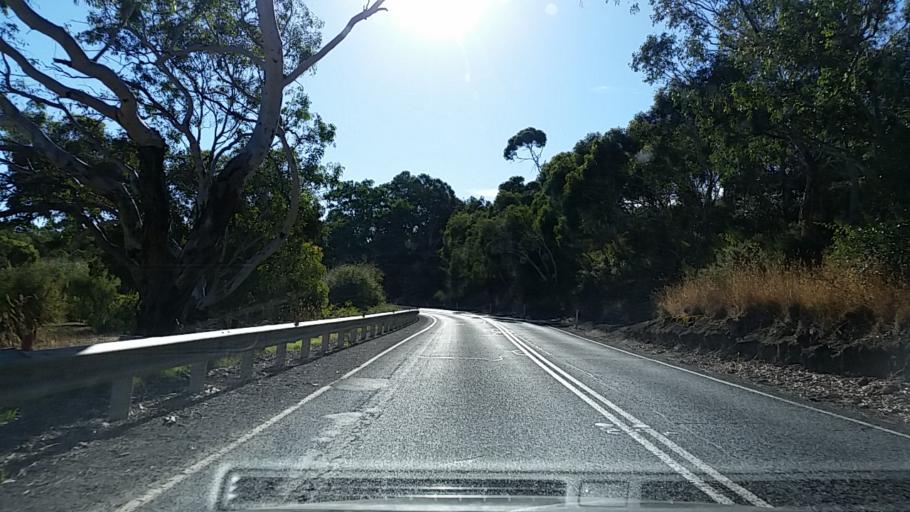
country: AU
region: South Australia
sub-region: Mount Barker
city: Nairne
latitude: -35.0389
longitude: 138.9233
